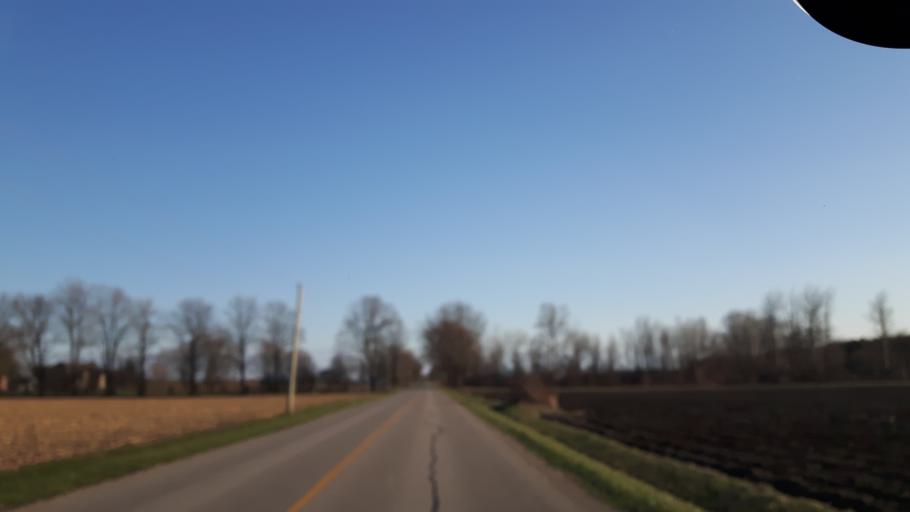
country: CA
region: Ontario
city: Goderich
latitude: 43.6814
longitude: -81.6848
